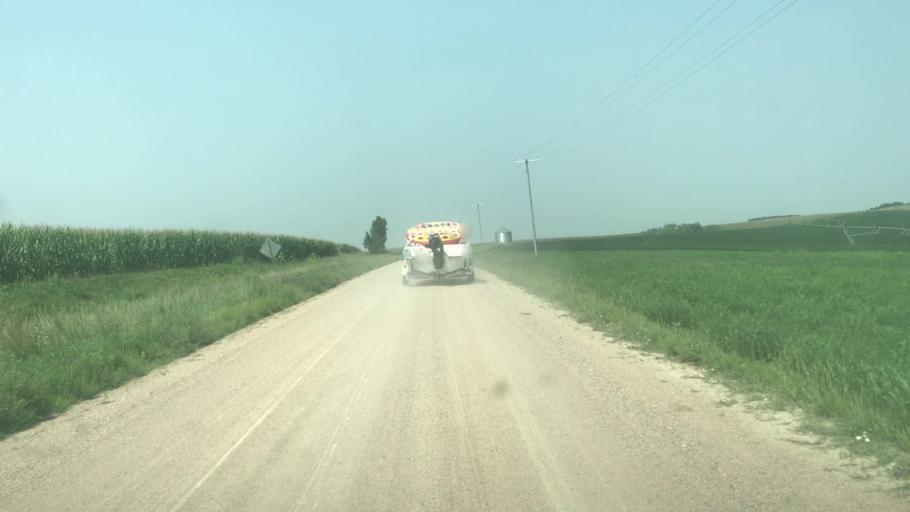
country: US
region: Nebraska
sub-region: Sherman County
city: Loup City
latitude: 41.2657
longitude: -98.9191
